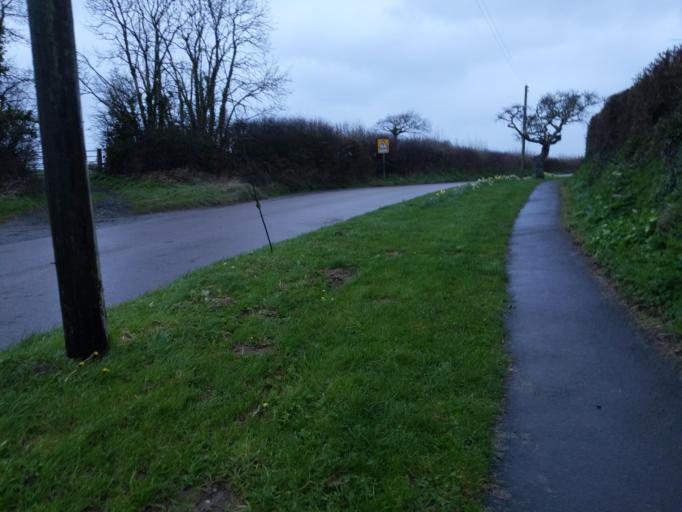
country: GB
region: England
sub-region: Devon
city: Wembury
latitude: 50.3208
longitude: -4.0342
